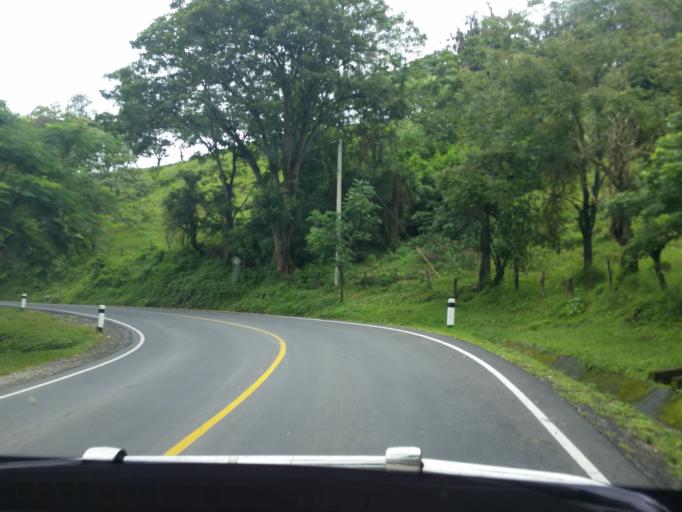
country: NI
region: Jinotega
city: Jinotega
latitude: 13.1418
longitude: -85.9629
